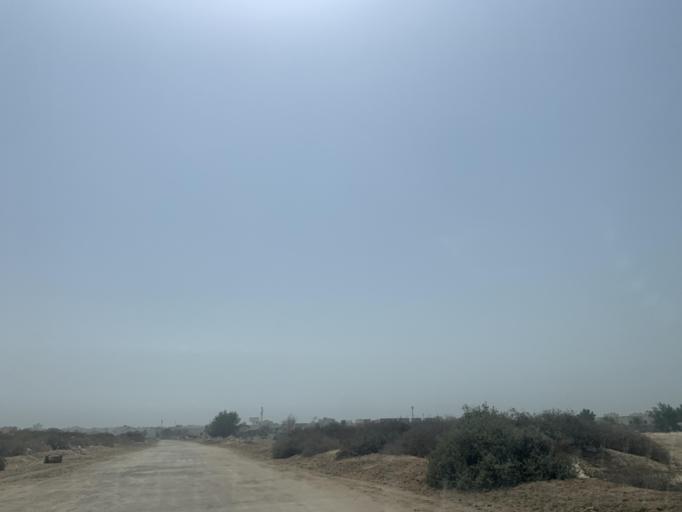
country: BH
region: Northern
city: Madinat `Isa
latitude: 26.1922
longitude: 50.5005
